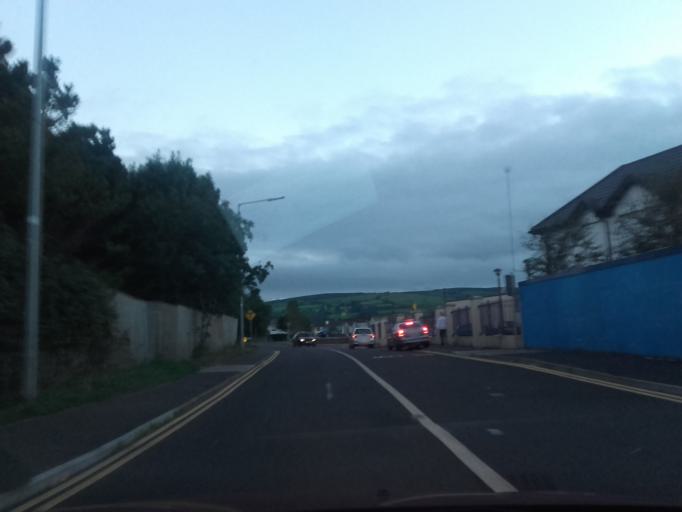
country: IE
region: Leinster
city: Tallaght
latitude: 53.2871
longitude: -6.3894
